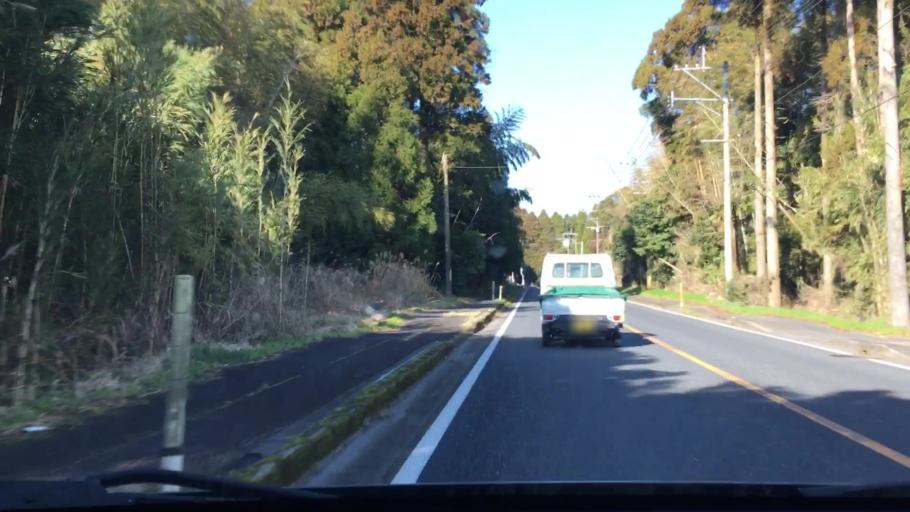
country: JP
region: Kagoshima
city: Kokubu-matsuki
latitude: 31.6716
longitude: 130.8634
